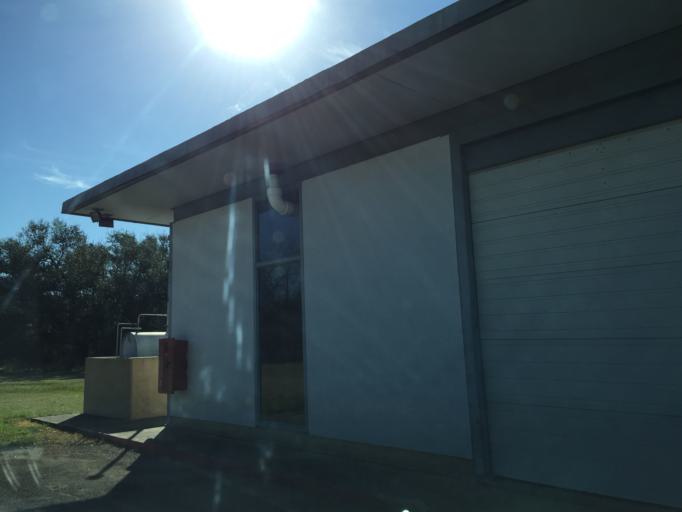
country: US
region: Texas
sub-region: Williamson County
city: Jollyville
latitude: 30.4374
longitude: -97.7526
